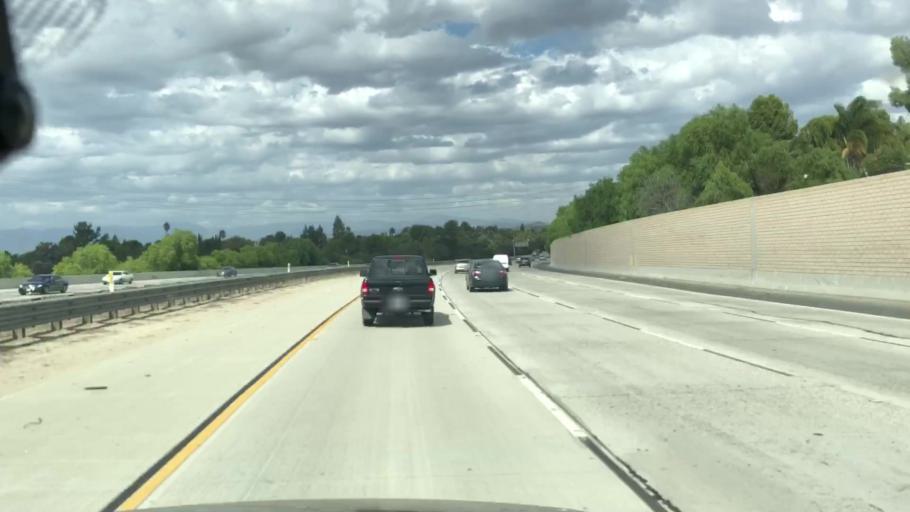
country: US
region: California
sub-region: Ventura County
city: Thousand Oaks
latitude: 34.1884
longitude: -118.8622
